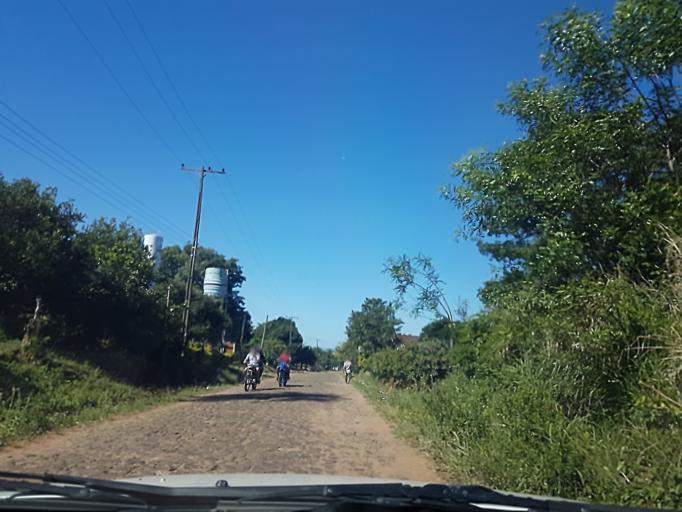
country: PY
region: Cordillera
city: Atyra
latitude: -25.2803
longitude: -57.1440
